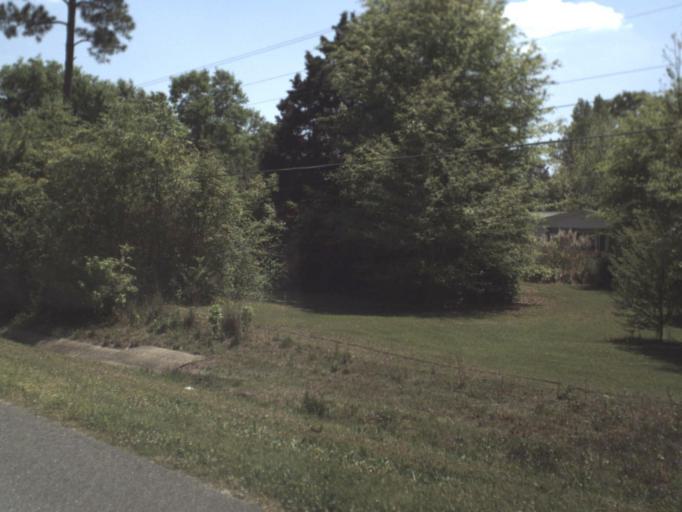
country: US
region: Florida
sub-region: Escambia County
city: Century
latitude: 30.9503
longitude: -87.1987
